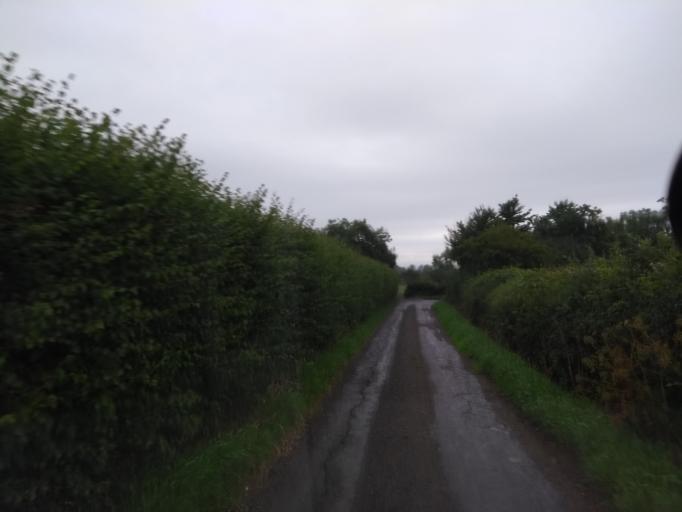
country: GB
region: England
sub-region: Somerset
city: Street
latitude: 51.0968
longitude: -2.7015
